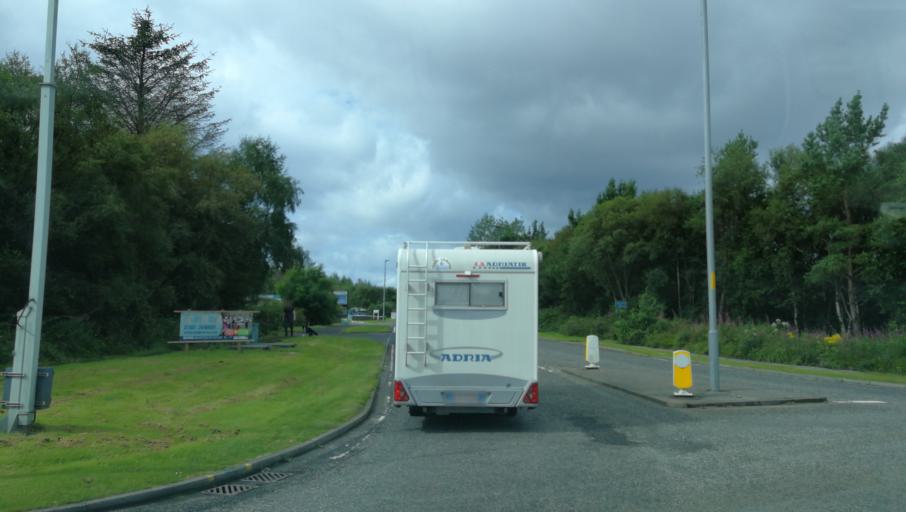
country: GB
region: Scotland
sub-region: Highland
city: Portree
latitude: 57.2725
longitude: -5.7447
